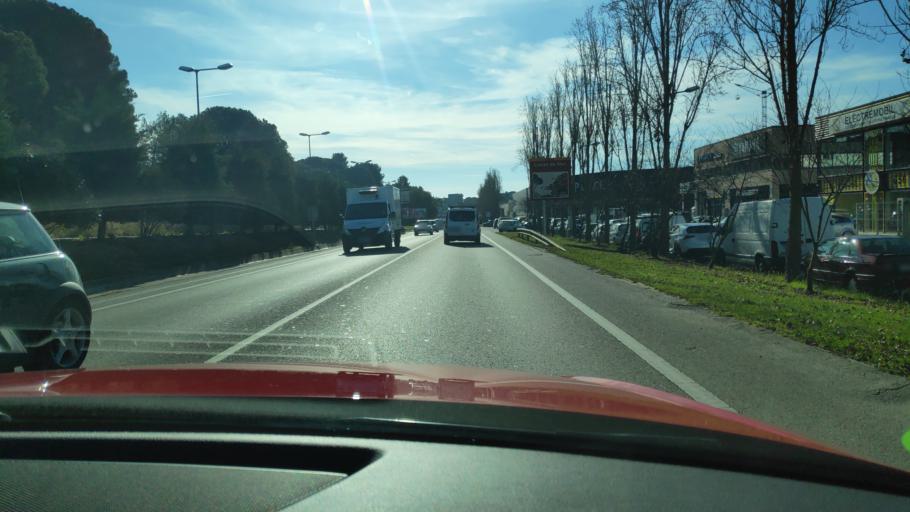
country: ES
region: Catalonia
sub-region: Provincia de Girona
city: Lloret de Mar
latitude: 41.7121
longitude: 2.8317
